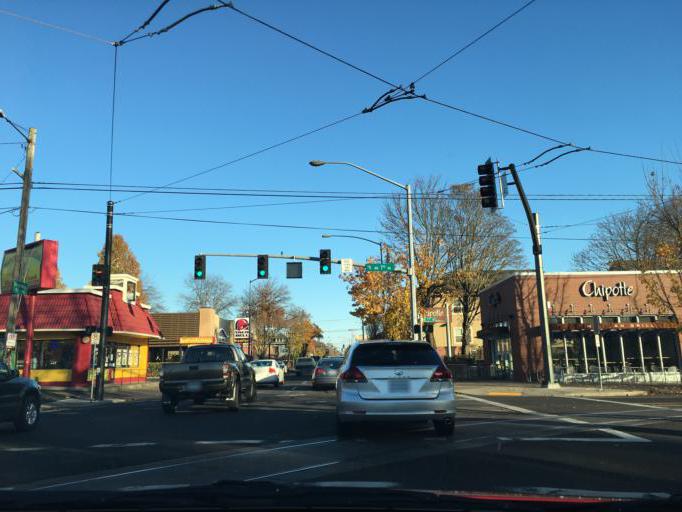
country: US
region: Oregon
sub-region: Multnomah County
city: Portland
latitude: 45.5344
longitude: -122.6588
